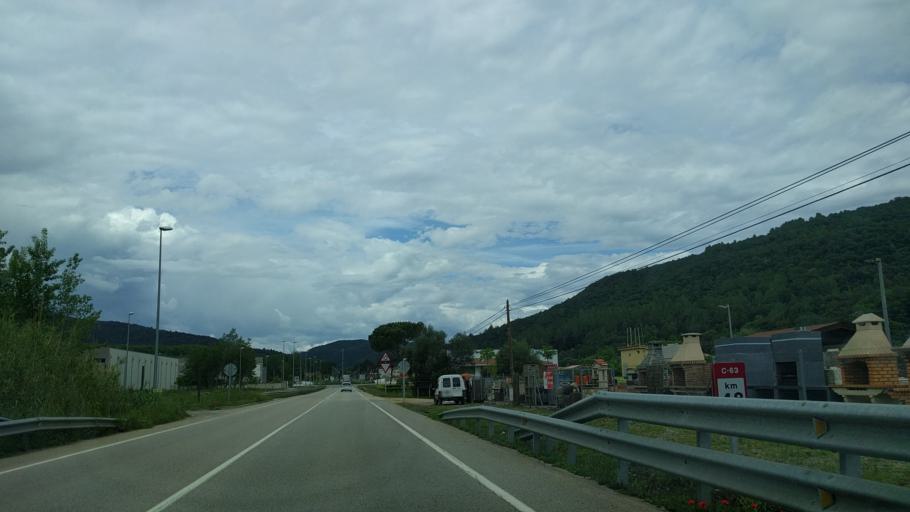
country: ES
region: Catalonia
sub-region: Provincia de Girona
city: la Cellera de Ter
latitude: 42.0174
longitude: 2.5967
